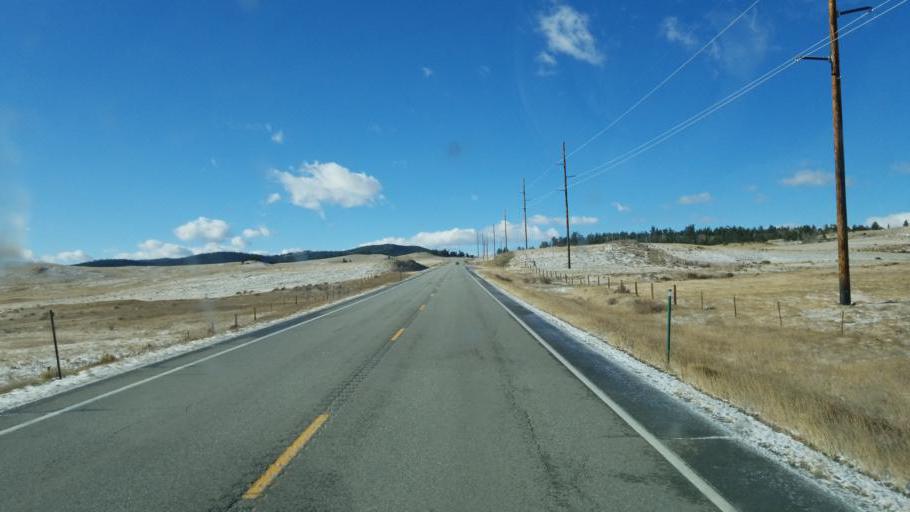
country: US
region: Colorado
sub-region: Park County
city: Fairplay
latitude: 39.3058
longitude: -105.8904
